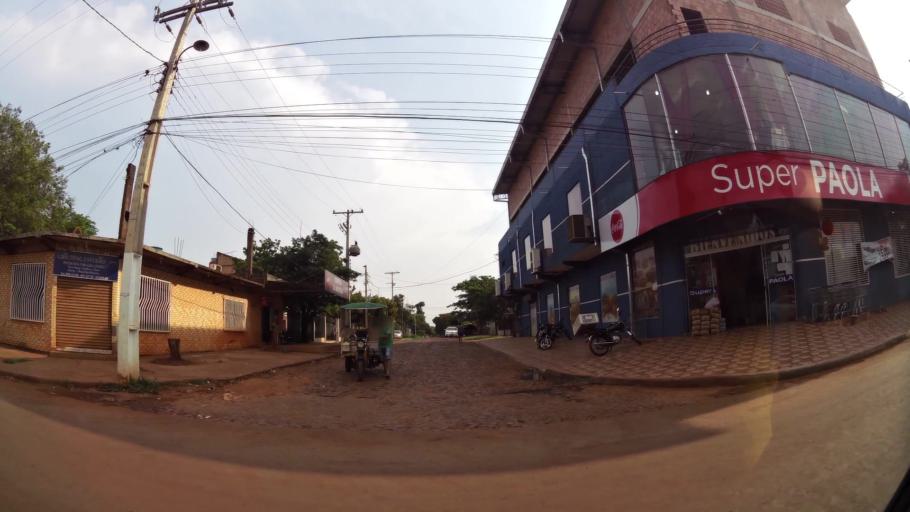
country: PY
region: Alto Parana
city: Ciudad del Este
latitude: -25.4826
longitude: -54.6524
